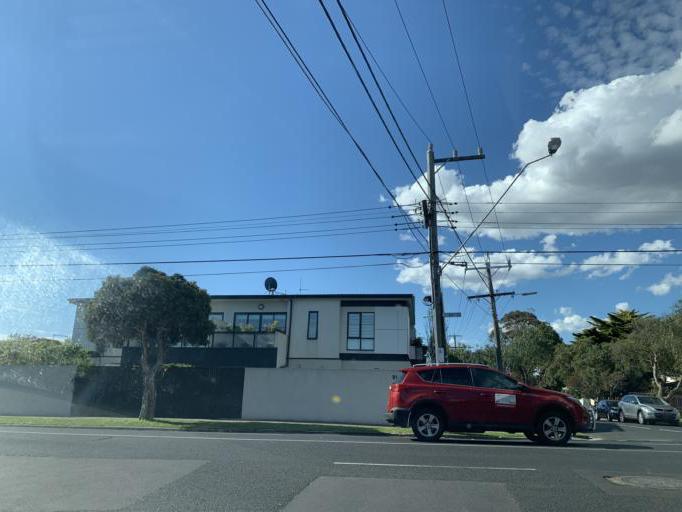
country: AU
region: Victoria
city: Hampton
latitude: -37.9530
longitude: 145.0129
